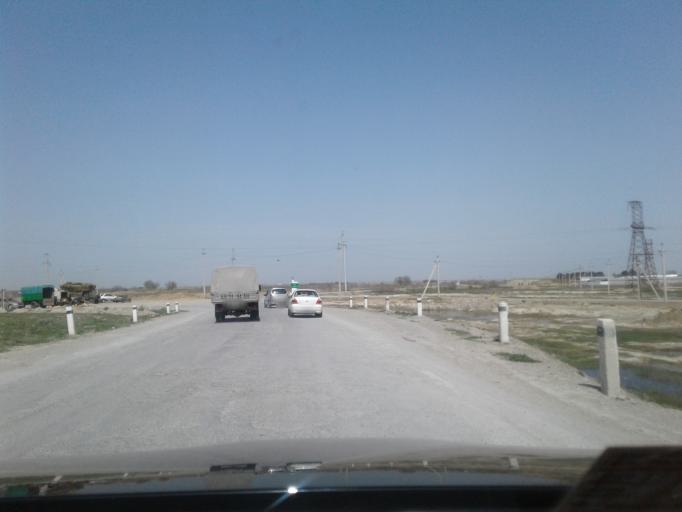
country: TM
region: Ahal
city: Abadan
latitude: 38.1764
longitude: 57.9813
